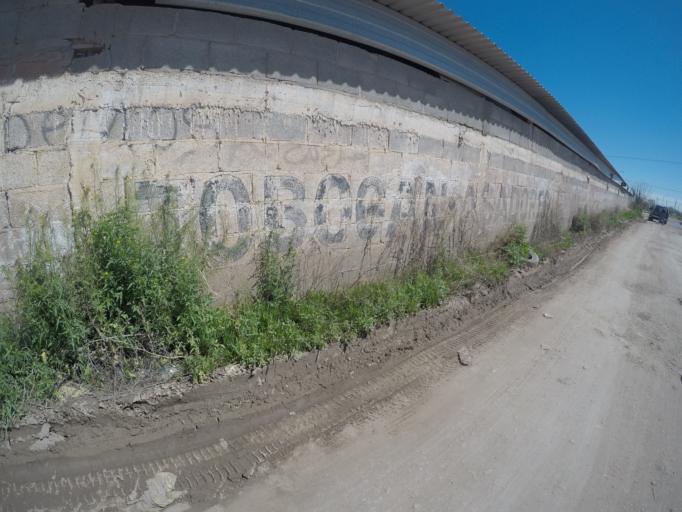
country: US
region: Texas
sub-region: El Paso County
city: Socorro Mission Number 1 Colonia
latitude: 31.6064
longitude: -106.3109
